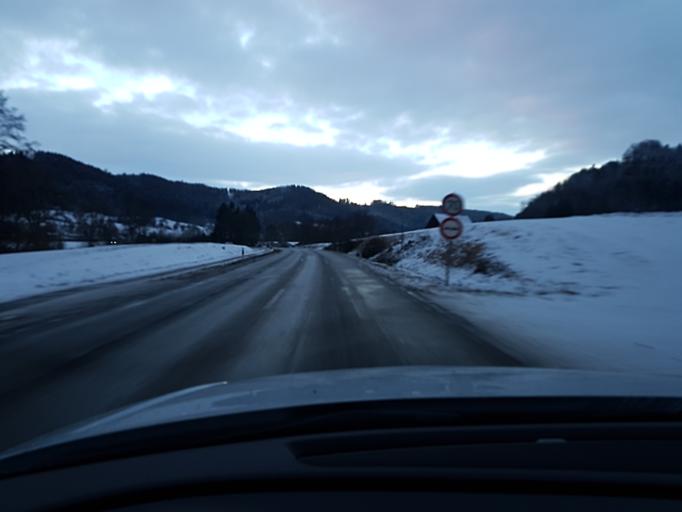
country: DE
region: Baden-Wuerttemberg
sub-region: Regierungsbezirk Stuttgart
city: Kaisersbach
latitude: 48.9742
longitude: 9.6372
